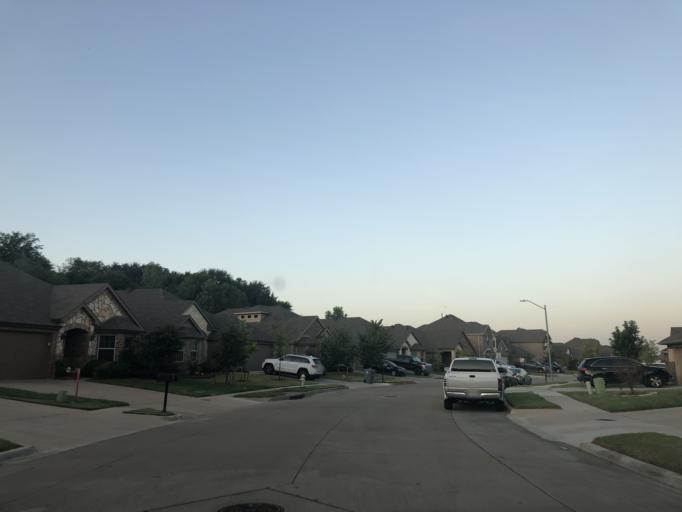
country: US
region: Texas
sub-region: Dallas County
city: Duncanville
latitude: 32.6584
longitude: -96.9644
